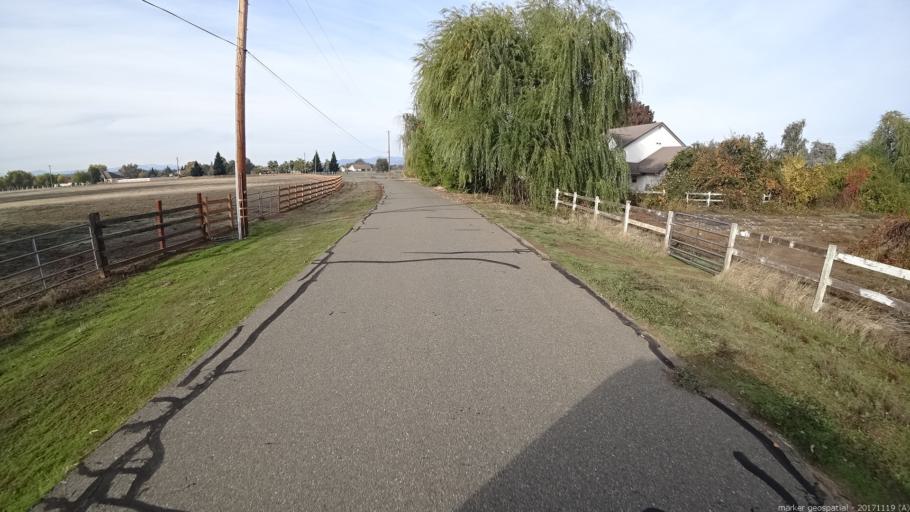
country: US
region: California
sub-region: Shasta County
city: Anderson
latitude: 40.5117
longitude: -122.3271
